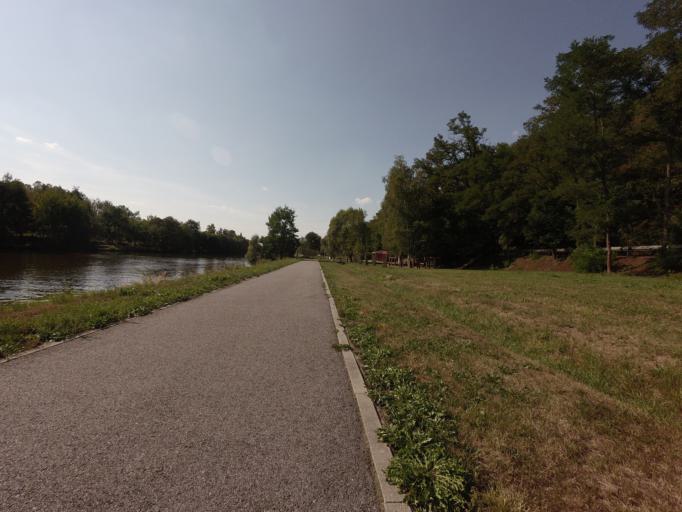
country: CZ
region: Jihocesky
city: Tyn nad Vltavou
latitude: 49.2137
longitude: 14.4389
